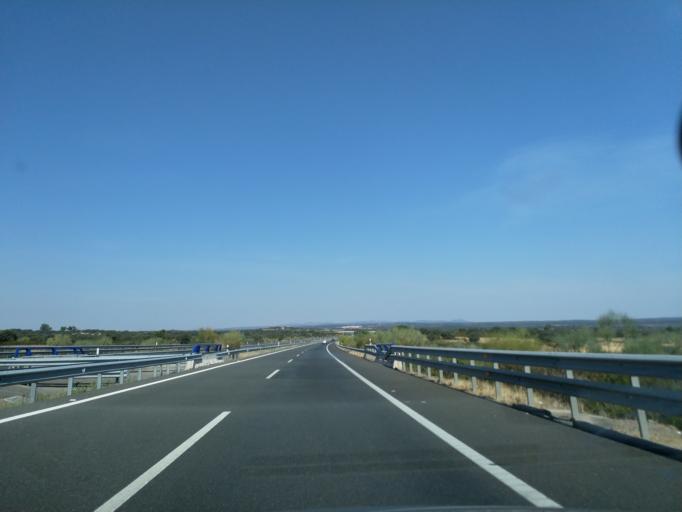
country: ES
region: Extremadura
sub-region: Provincia de Caceres
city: Alcuescar
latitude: 39.1822
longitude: -6.2747
